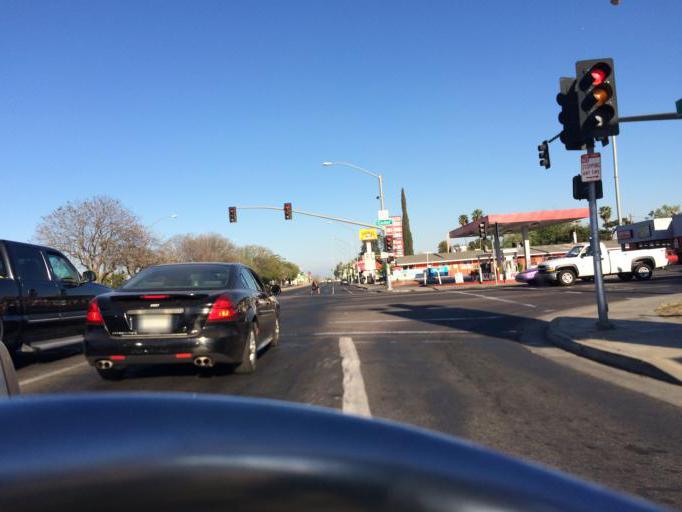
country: US
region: California
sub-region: Fresno County
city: Fresno
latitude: 36.7358
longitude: -119.7549
